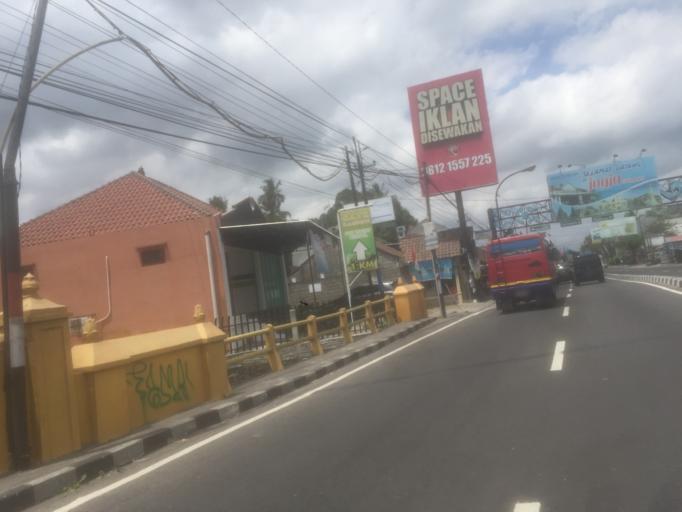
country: ID
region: Daerah Istimewa Yogyakarta
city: Sleman
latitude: -7.6497
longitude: 110.3249
